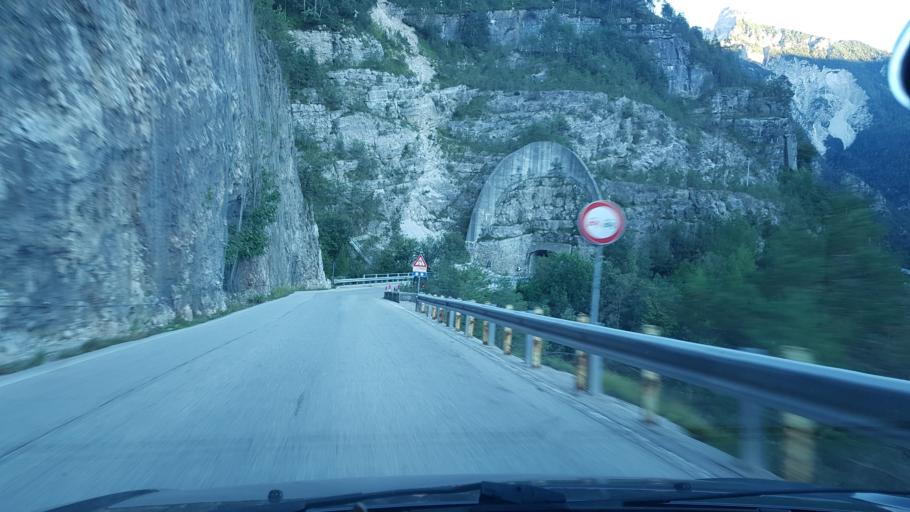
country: IT
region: Veneto
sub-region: Provincia di Belluno
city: Forno di Zoldo
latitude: 46.3379
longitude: 12.2269
